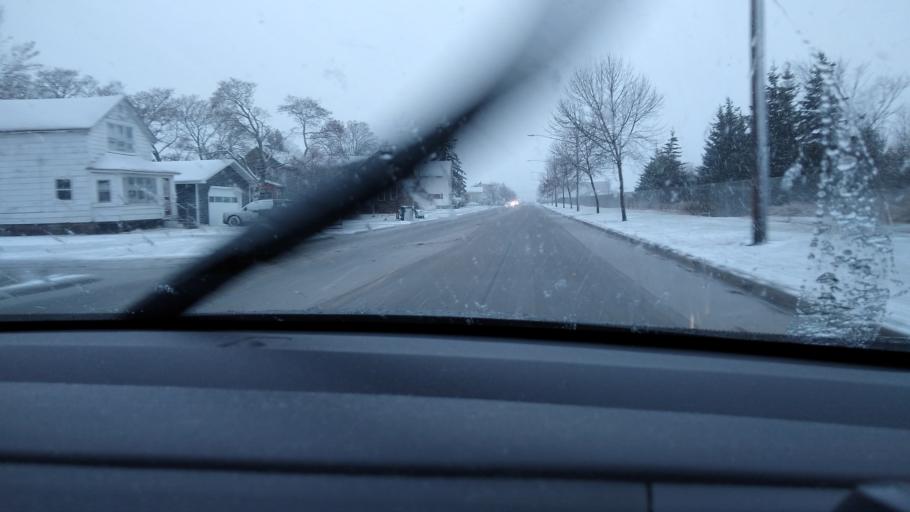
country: US
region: Michigan
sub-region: Delta County
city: Escanaba
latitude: 45.7493
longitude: -87.0633
